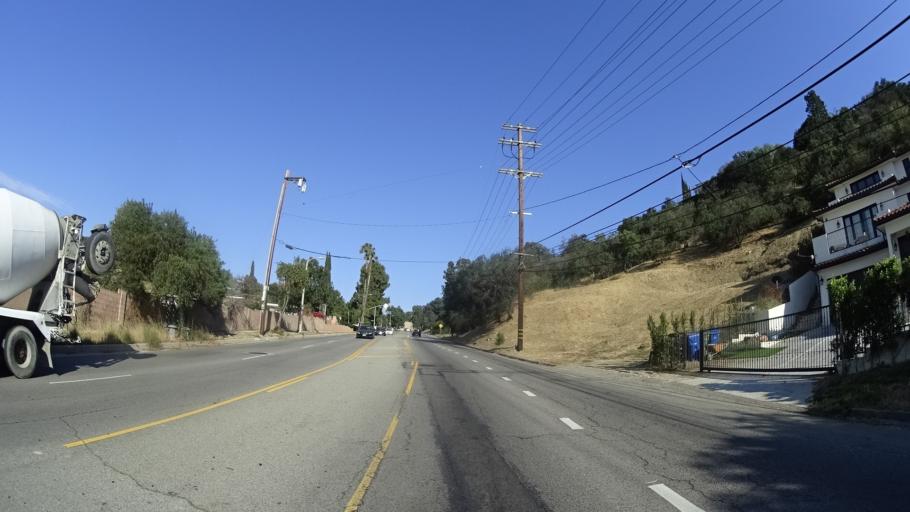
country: US
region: California
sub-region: Los Angeles County
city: Universal City
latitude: 34.1257
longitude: -118.3789
